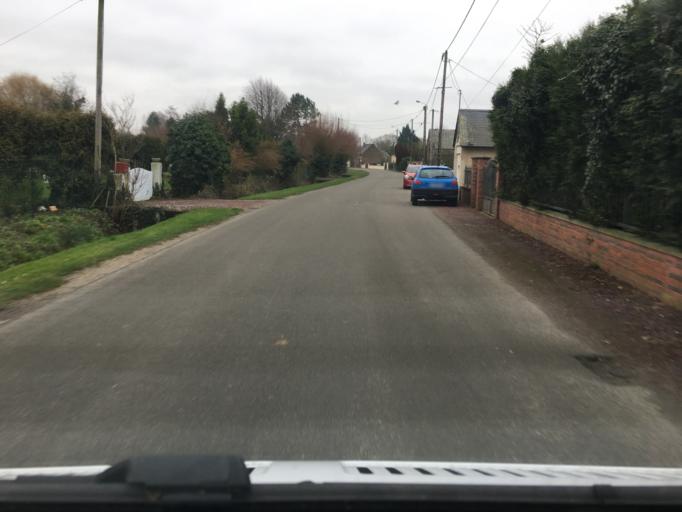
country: FR
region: Picardie
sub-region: Departement de la Somme
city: Pende
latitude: 50.1640
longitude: 1.5549
